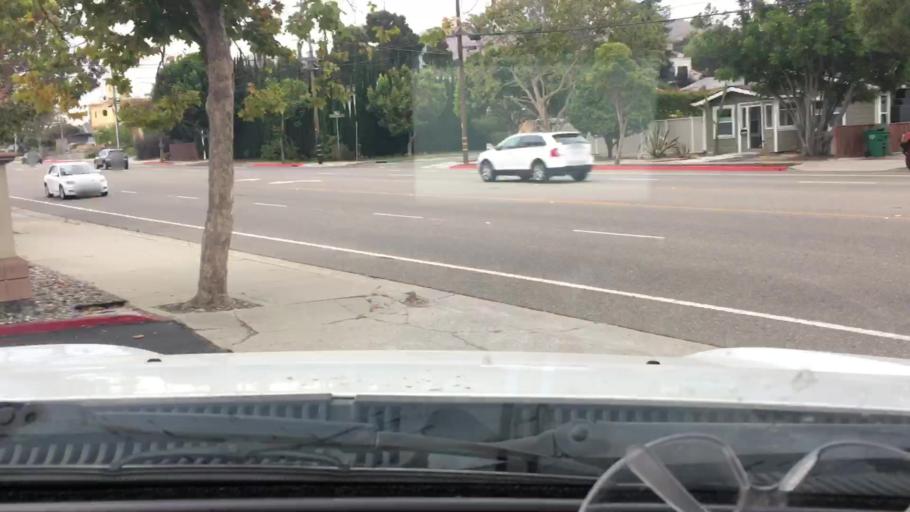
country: US
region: California
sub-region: San Luis Obispo County
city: San Luis Obispo
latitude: 35.2647
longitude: -120.6523
